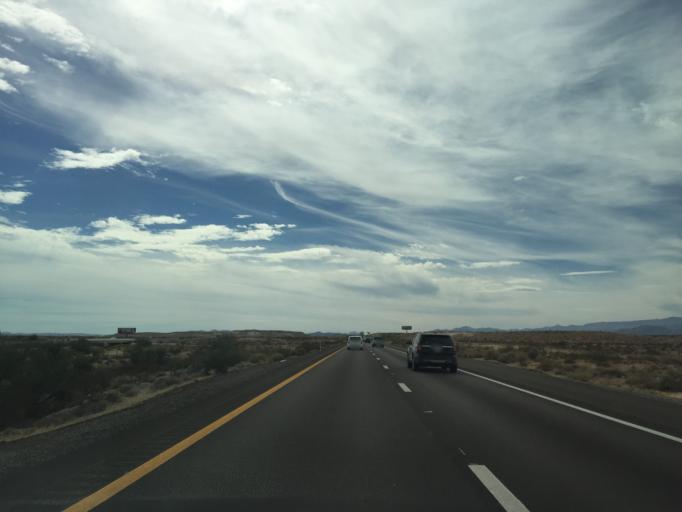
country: US
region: Nevada
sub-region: Clark County
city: Moapa Town
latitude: 36.5580
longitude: -114.6899
